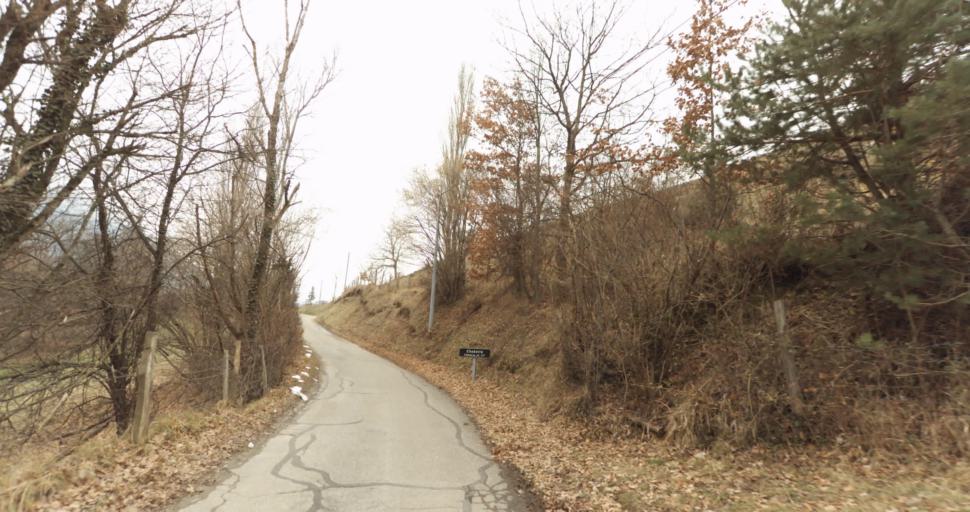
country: FR
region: Rhone-Alpes
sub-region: Departement de l'Isere
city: Saint-Georges-de-Commiers
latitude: 45.0253
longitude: 5.6889
